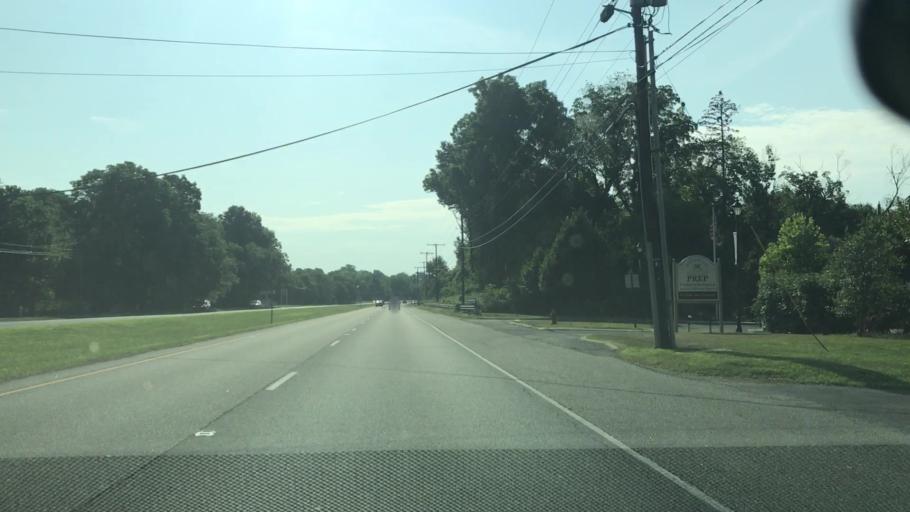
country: US
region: New Jersey
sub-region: Hunterdon County
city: Whitehouse Station
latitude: 40.6188
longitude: -74.7546
